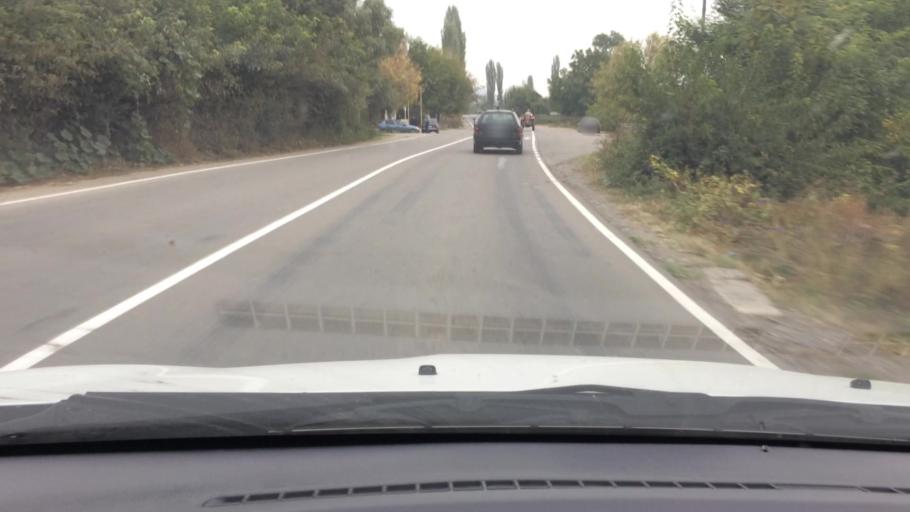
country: GE
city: Naghvarevi
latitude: 41.3254
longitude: 44.8004
